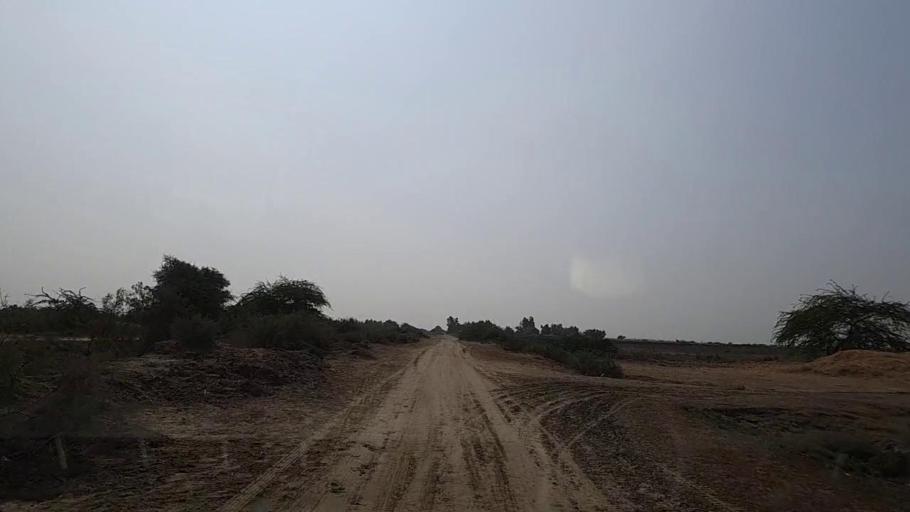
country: PK
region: Sindh
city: Mirpur Sakro
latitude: 24.5510
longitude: 67.7916
